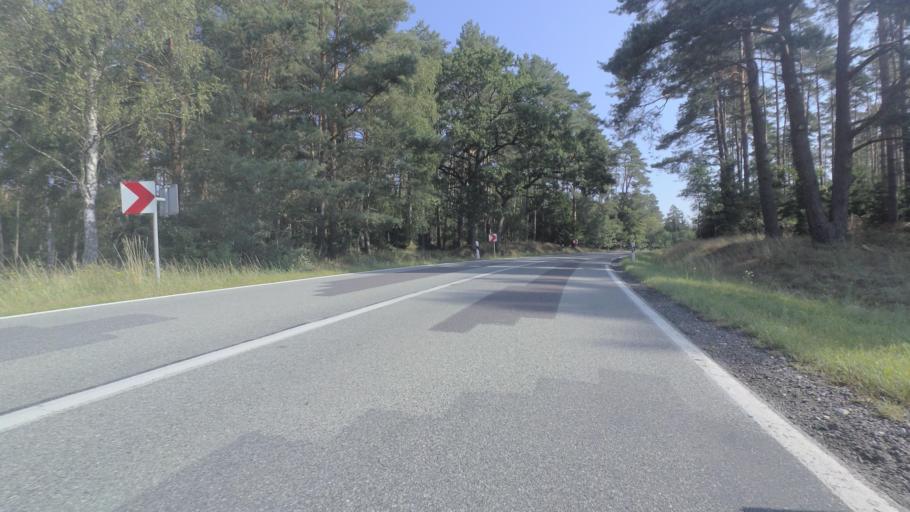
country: DE
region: Mecklenburg-Vorpommern
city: Malchow
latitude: 53.5458
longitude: 12.4349
